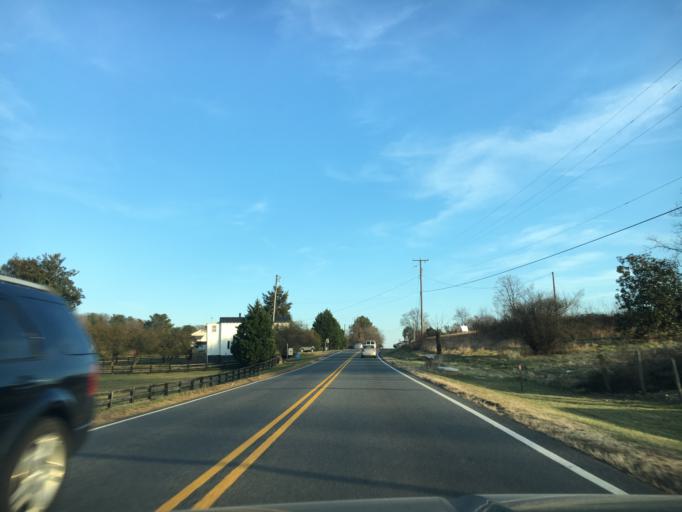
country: US
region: Virginia
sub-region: Culpeper County
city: Merrimac
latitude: 38.5131
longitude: -78.0661
